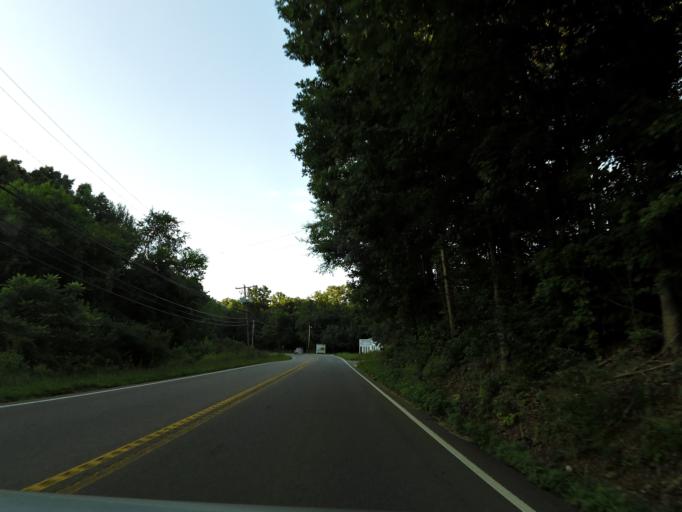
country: US
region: Tennessee
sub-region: Loudon County
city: Lenoir City
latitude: 35.8137
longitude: -84.2534
